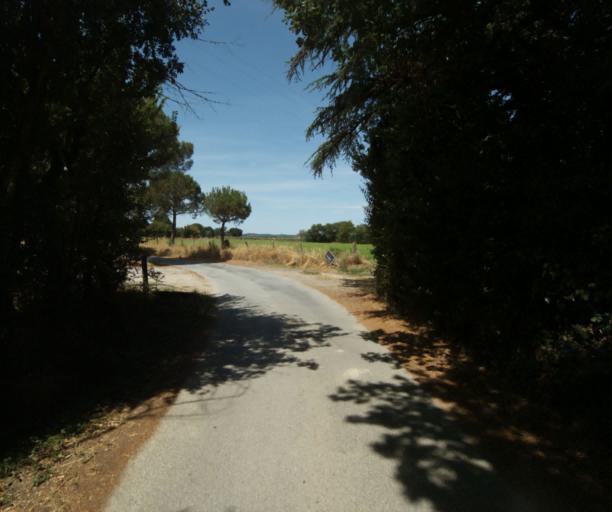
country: FR
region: Midi-Pyrenees
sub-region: Departement de la Haute-Garonne
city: Revel
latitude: 43.5053
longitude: 2.0316
